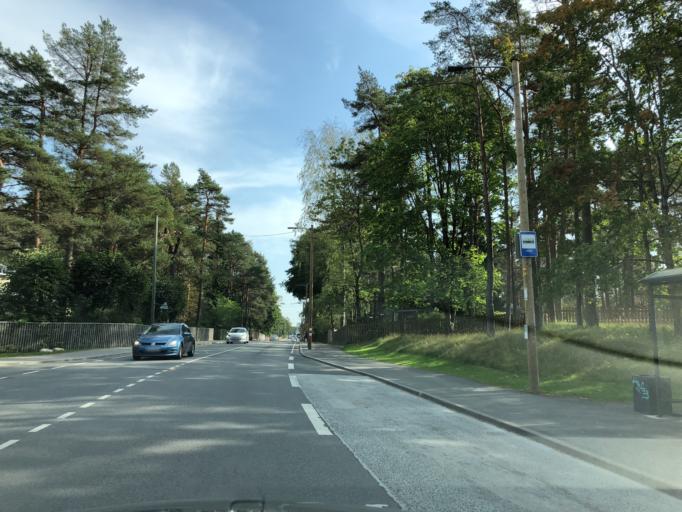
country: EE
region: Harju
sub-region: Tallinna linn
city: Tallinn
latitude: 59.3781
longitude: 24.7047
